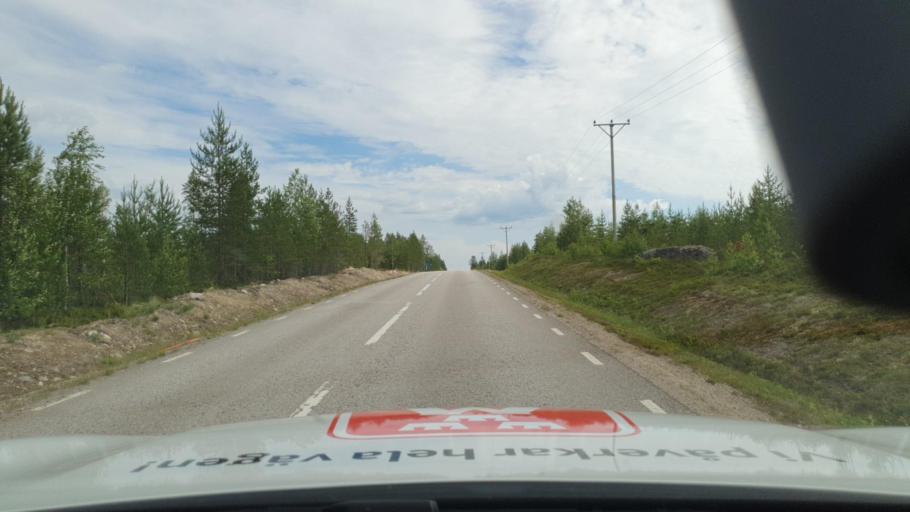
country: NO
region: Hedmark
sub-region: Trysil
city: Innbygda
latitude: 60.9854
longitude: 12.4927
